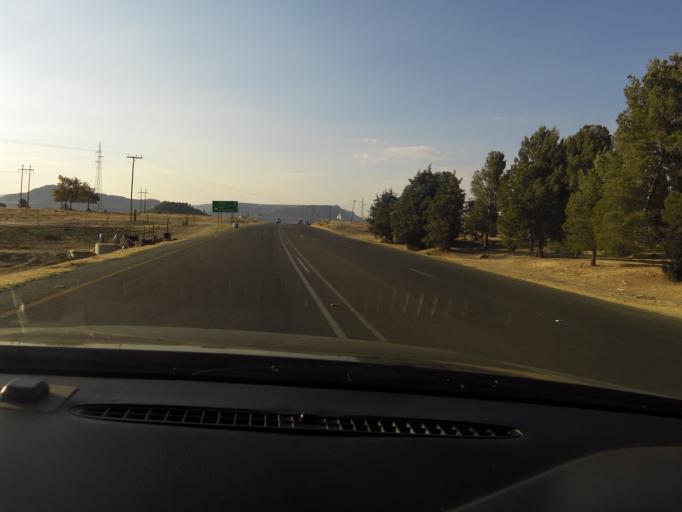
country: LS
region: Maseru
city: Nako
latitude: -29.5946
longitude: 27.4961
